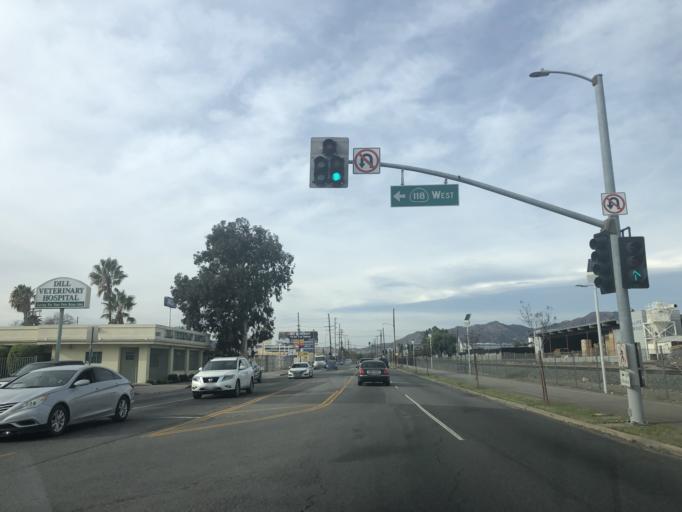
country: US
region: California
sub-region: Los Angeles County
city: San Fernando
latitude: 34.2732
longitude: -118.4296
